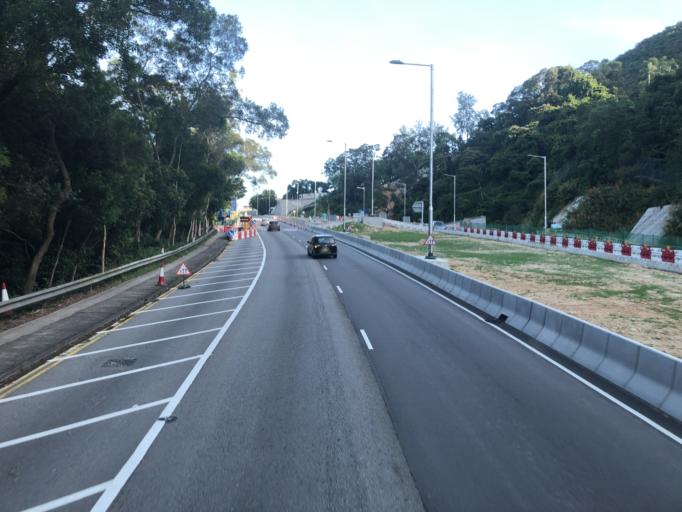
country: HK
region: Sai Kung
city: Sai Kung
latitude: 22.3453
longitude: 114.2560
